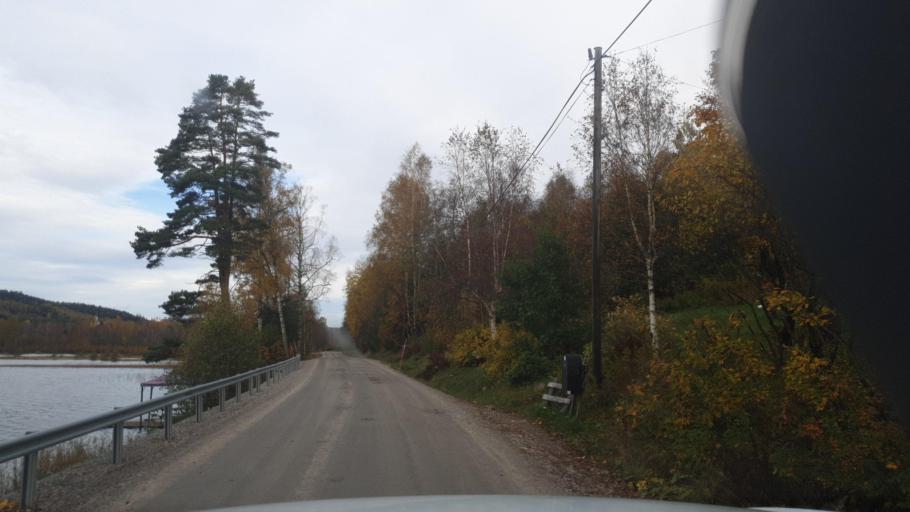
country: SE
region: Vaermland
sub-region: Arvika Kommun
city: Arvika
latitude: 59.7437
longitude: 12.8307
